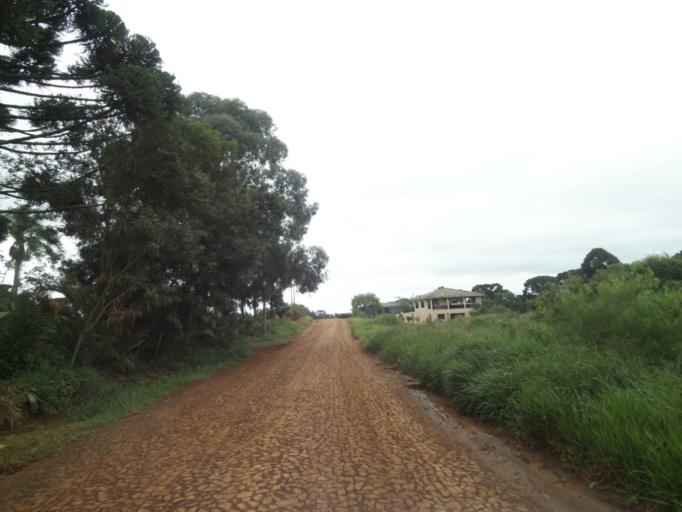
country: BR
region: Parana
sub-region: Pitanga
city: Pitanga
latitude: -24.9360
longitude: -51.8671
